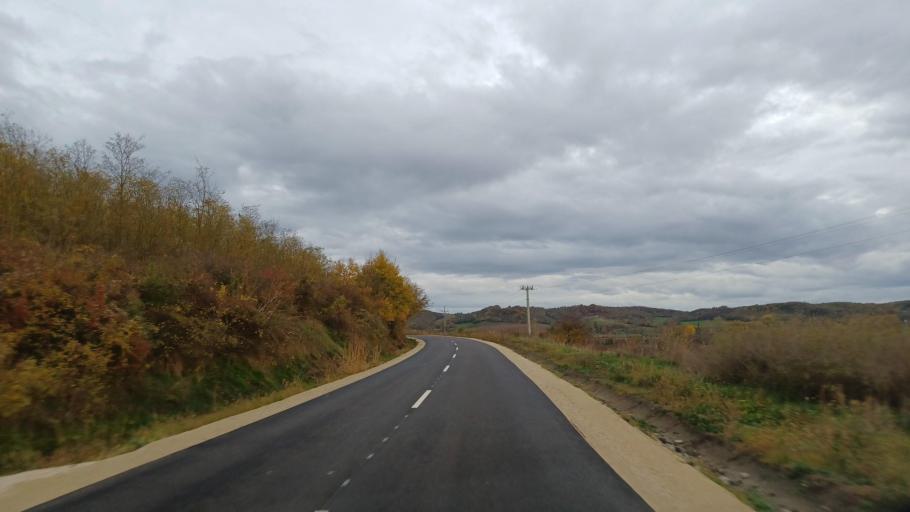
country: HU
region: Tolna
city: Gyonk
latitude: 46.5928
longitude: 18.4305
